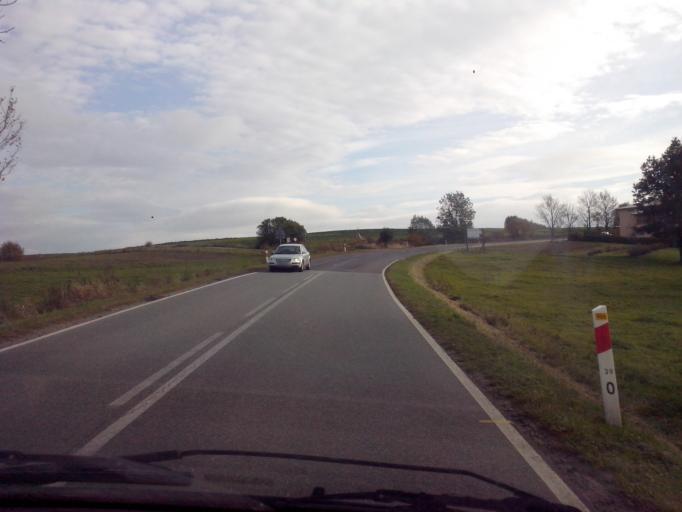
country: PL
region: Subcarpathian Voivodeship
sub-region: Powiat ropczycko-sedziszowski
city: Wielopole Skrzynskie
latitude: 49.9184
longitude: 21.6145
